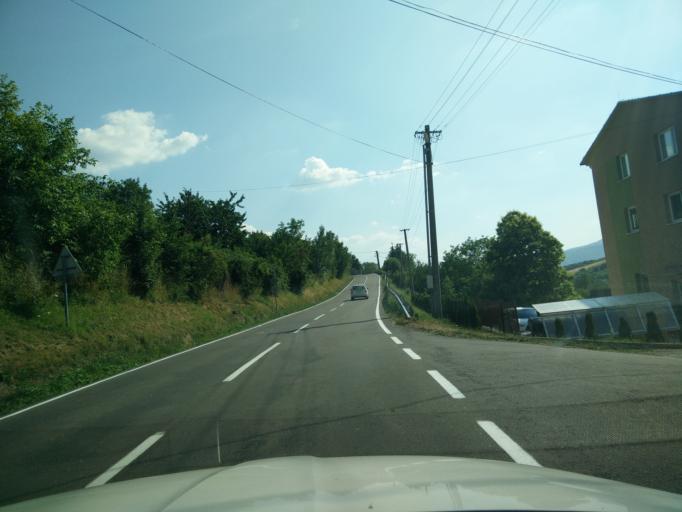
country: SK
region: Nitriansky
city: Bojnice
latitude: 48.8032
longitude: 18.5371
